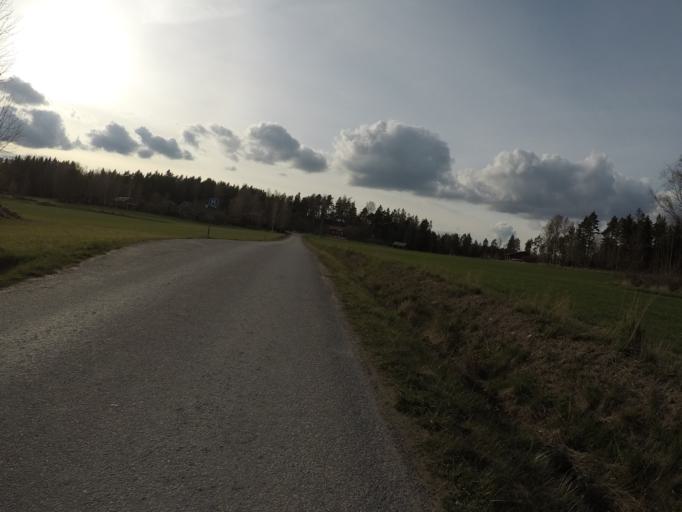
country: SE
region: Soedermanland
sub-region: Eskilstuna Kommun
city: Torshalla
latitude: 59.4326
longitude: 16.5135
